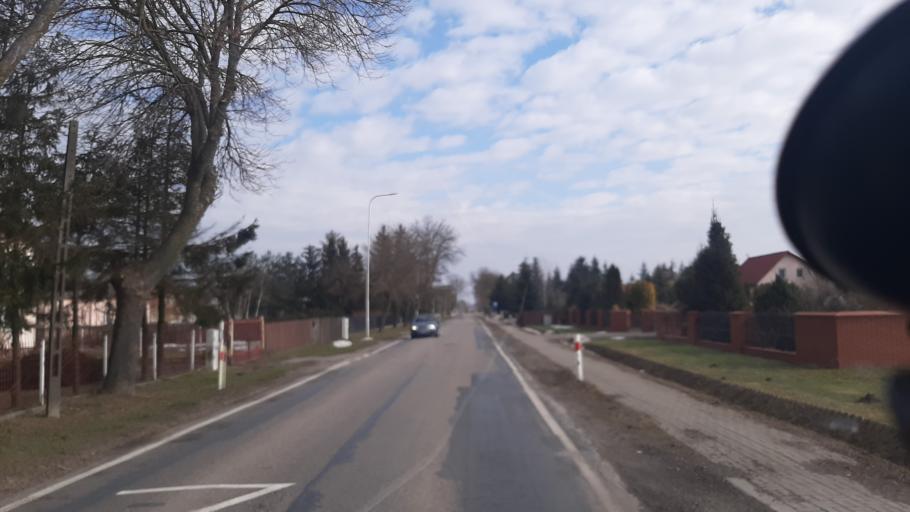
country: PL
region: Lublin Voivodeship
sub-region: Powiat lubelski
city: Niemce
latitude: 51.3615
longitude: 22.5765
